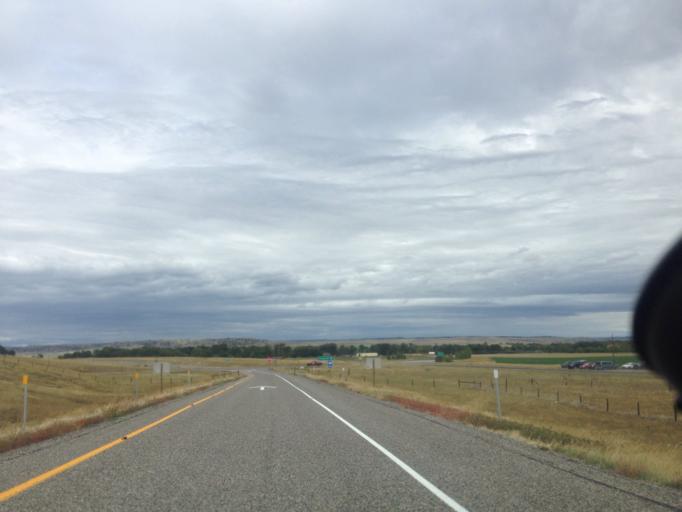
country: US
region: Montana
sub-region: Sweet Grass County
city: Big Timber
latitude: 45.7679
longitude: -109.7919
